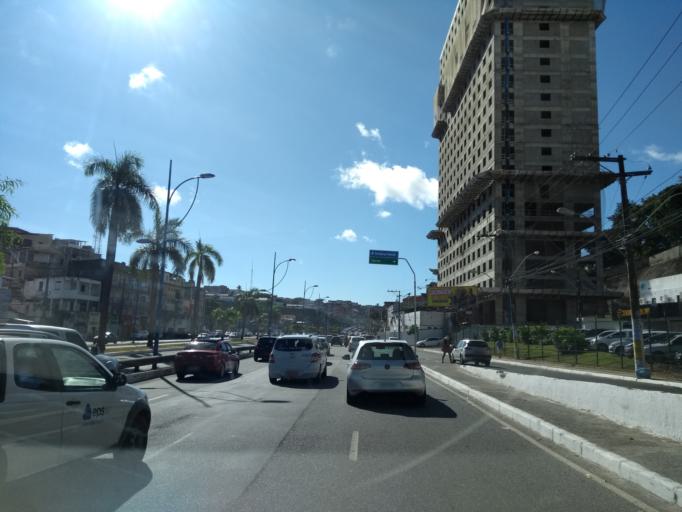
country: BR
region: Bahia
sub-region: Salvador
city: Salvador
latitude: -12.9970
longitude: -38.4930
